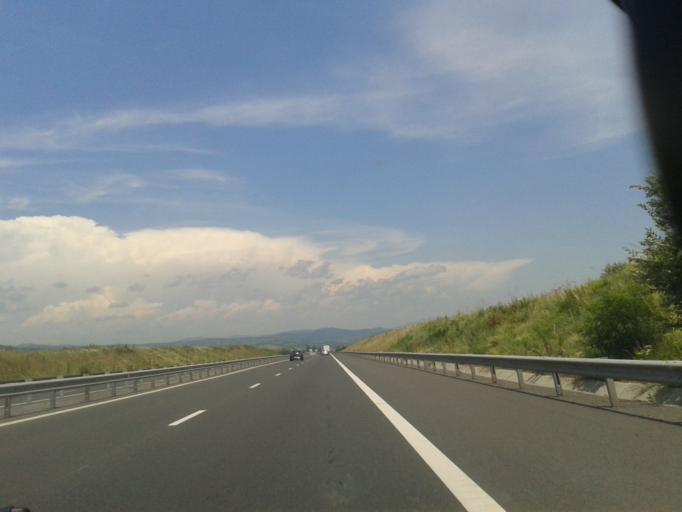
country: RO
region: Hunedoara
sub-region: Comuna Turdas
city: Turdas
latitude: 45.8517
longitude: 23.1371
